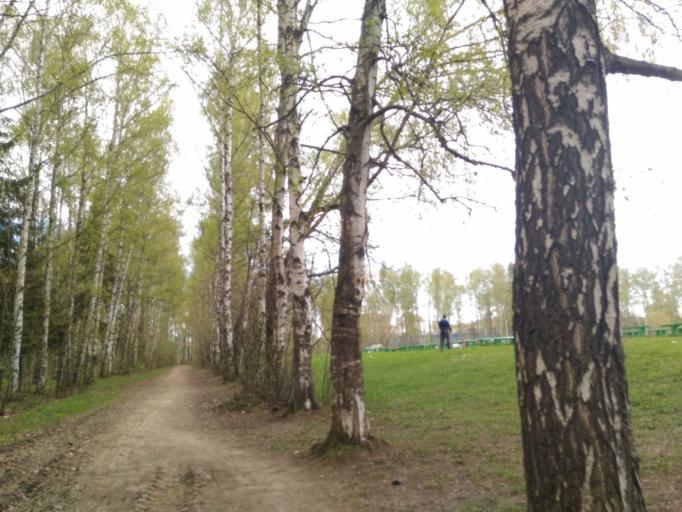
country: RU
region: Moskovskaya
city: Nakhabino
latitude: 55.8433
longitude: 37.1681
